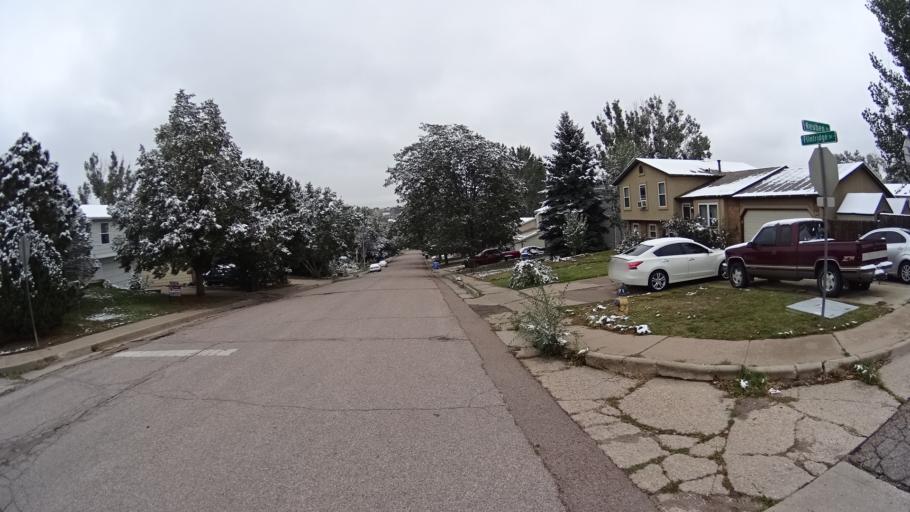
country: US
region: Colorado
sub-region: El Paso County
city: Cimarron Hills
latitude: 38.9268
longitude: -104.7676
